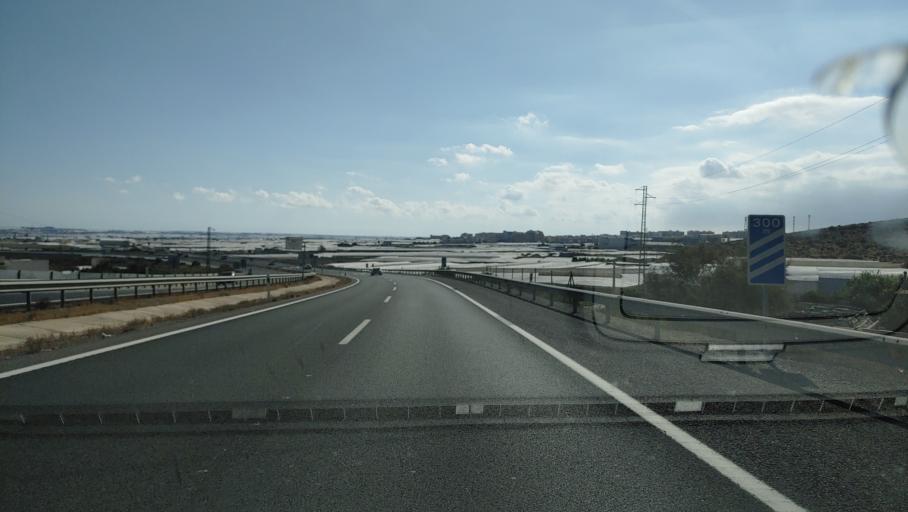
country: ES
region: Andalusia
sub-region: Provincia de Almeria
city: Aguadulce
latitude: 36.8128
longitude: -2.6017
